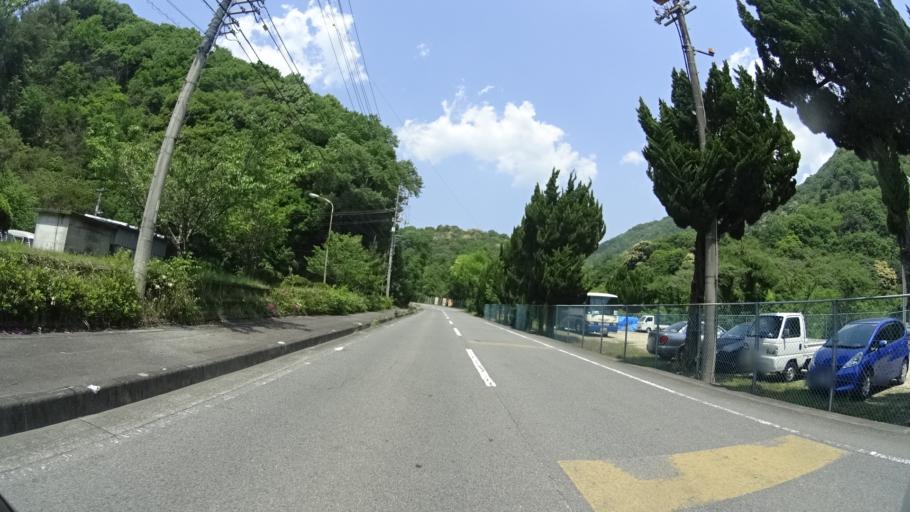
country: JP
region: Ehime
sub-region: Shikoku-chuo Shi
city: Matsuyama
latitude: 33.8670
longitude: 132.8265
